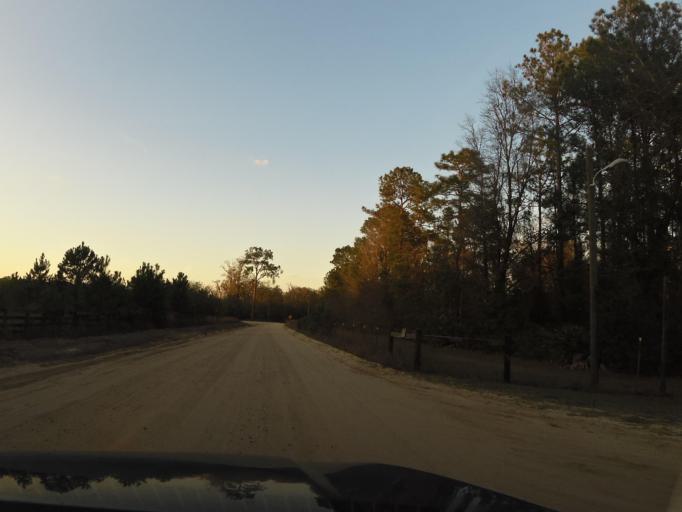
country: US
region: Florida
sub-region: Clay County
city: Green Cove Springs
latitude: 29.8680
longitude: -81.7965
